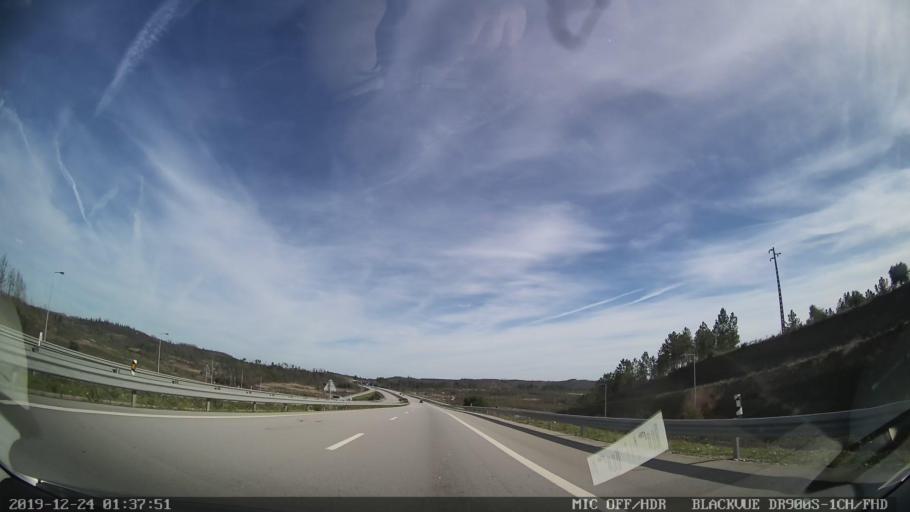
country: PT
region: Santarem
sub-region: Macao
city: Macao
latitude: 39.5296
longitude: -7.9506
